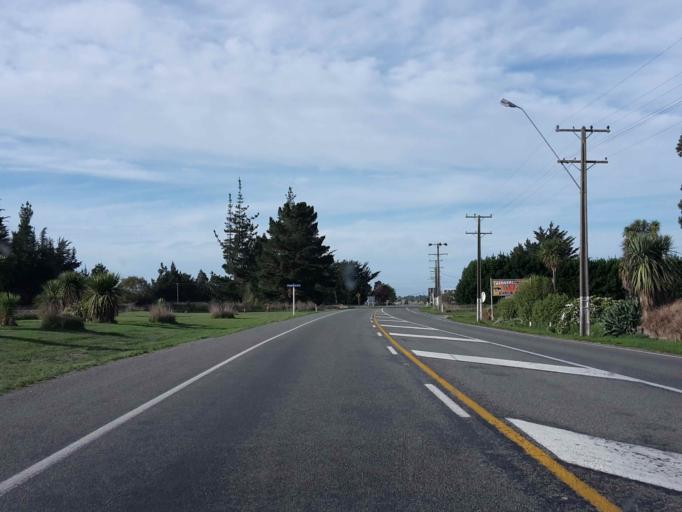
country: NZ
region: Canterbury
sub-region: Timaru District
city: Pleasant Point
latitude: -44.0670
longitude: 171.3704
